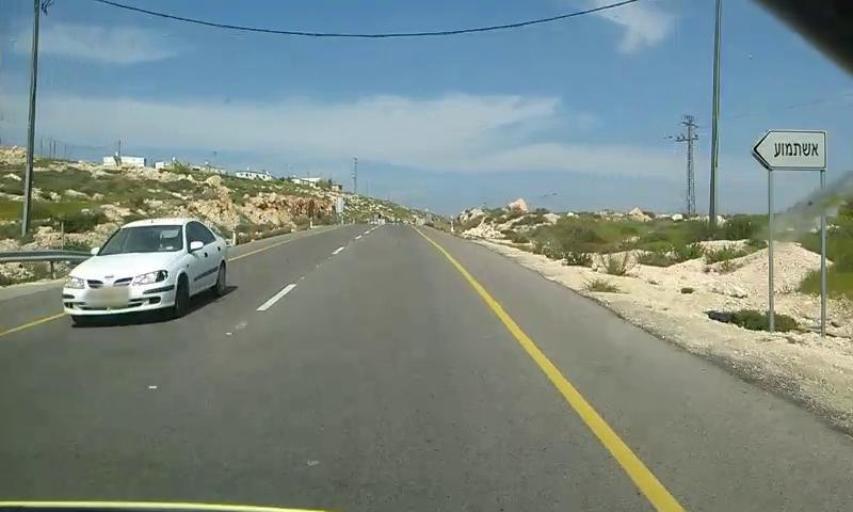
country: PS
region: West Bank
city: Az Zahiriyah
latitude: 31.3912
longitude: 35.0153
